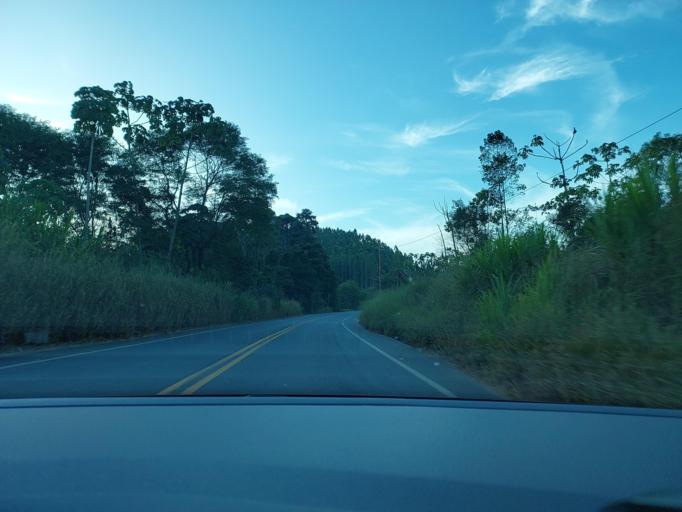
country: BR
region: Minas Gerais
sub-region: Vicosa
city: Vicosa
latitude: -20.8143
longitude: -42.8277
